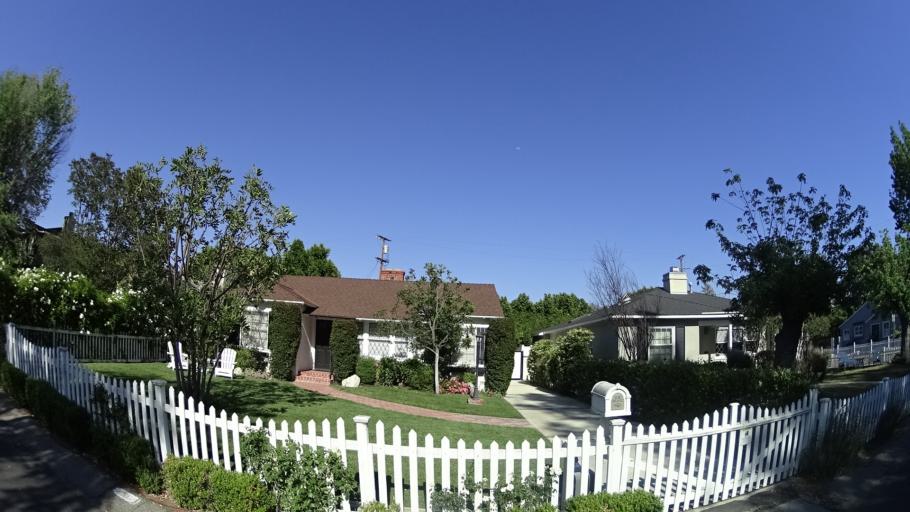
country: US
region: California
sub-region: Los Angeles County
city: North Hollywood
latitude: 34.1524
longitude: -118.3889
